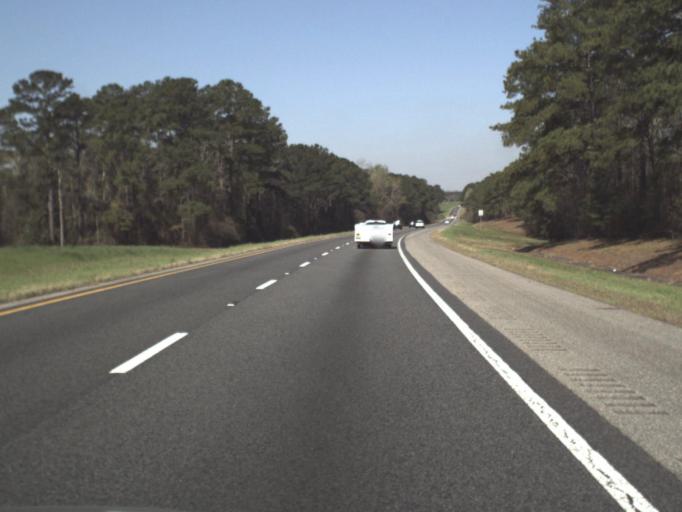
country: US
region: Florida
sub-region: Gadsden County
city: Gretna
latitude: 30.5811
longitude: -84.7072
